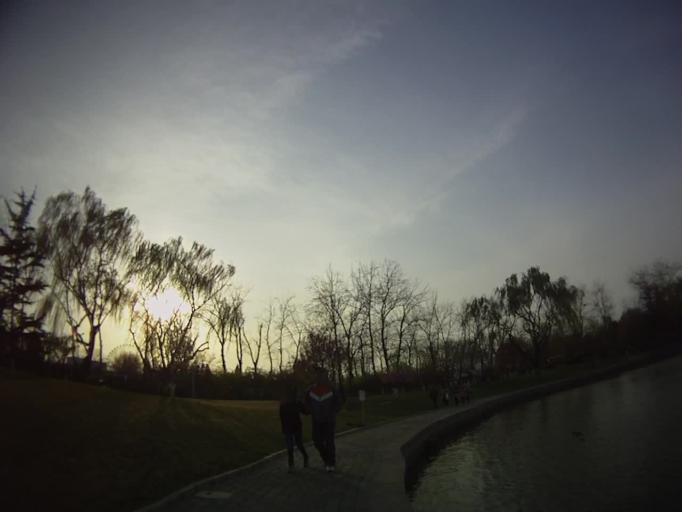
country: CN
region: Beijing
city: Longtan
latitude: 39.8771
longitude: 116.4316
